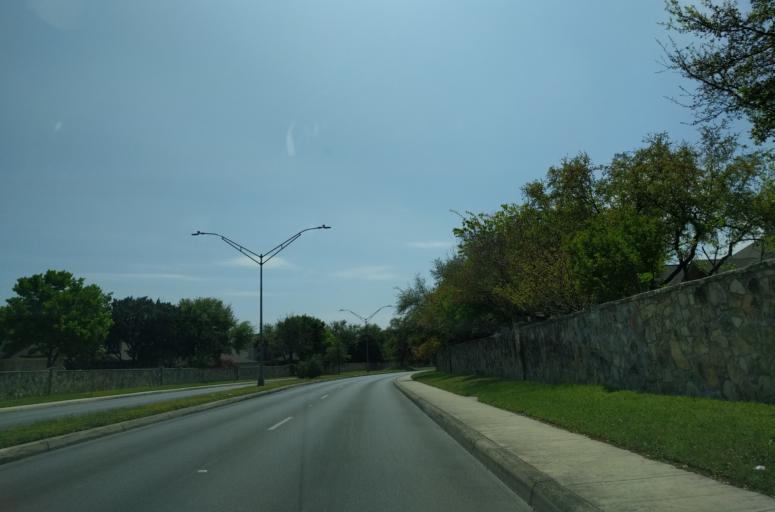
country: US
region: Texas
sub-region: Bexar County
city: Shavano Park
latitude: 29.5699
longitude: -98.5856
